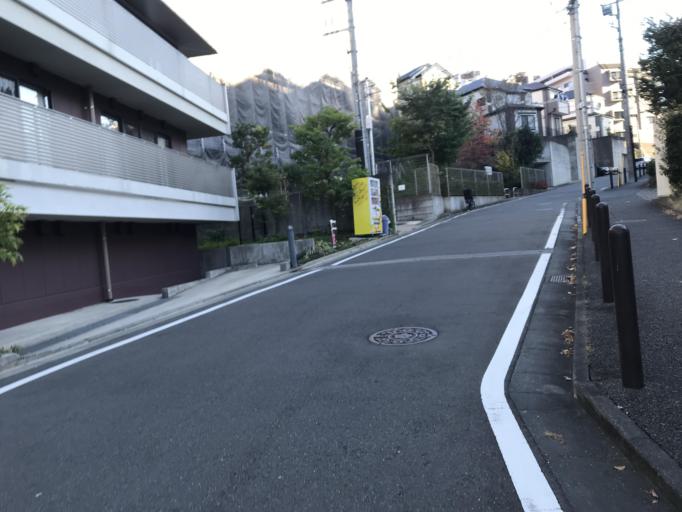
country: JP
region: Kanagawa
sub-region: Kawasaki-shi
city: Kawasaki
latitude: 35.5620
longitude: 139.6173
